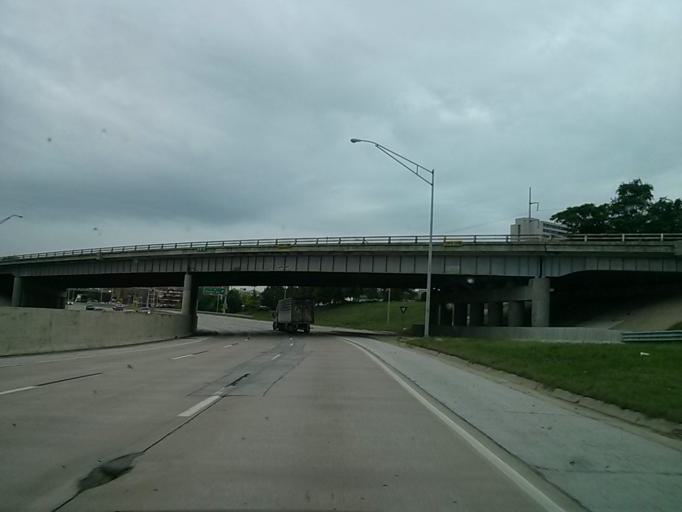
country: US
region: Oklahoma
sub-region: Tulsa County
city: Tulsa
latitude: 36.1449
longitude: -95.9937
